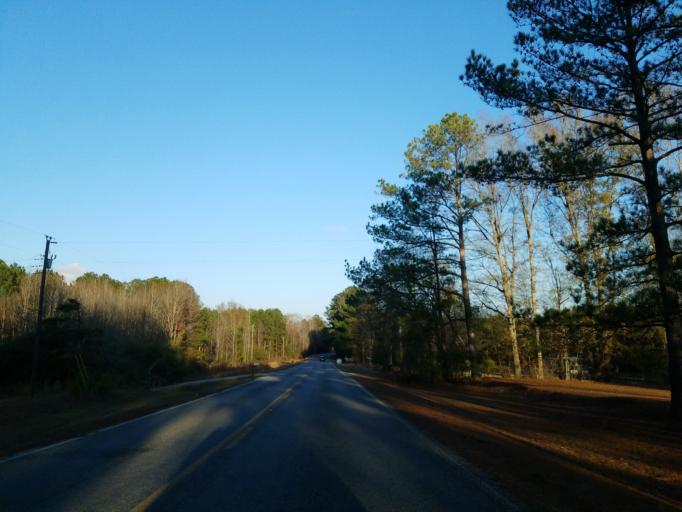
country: US
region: Mississippi
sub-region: Clarke County
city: Stonewall
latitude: 32.1651
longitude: -88.8609
